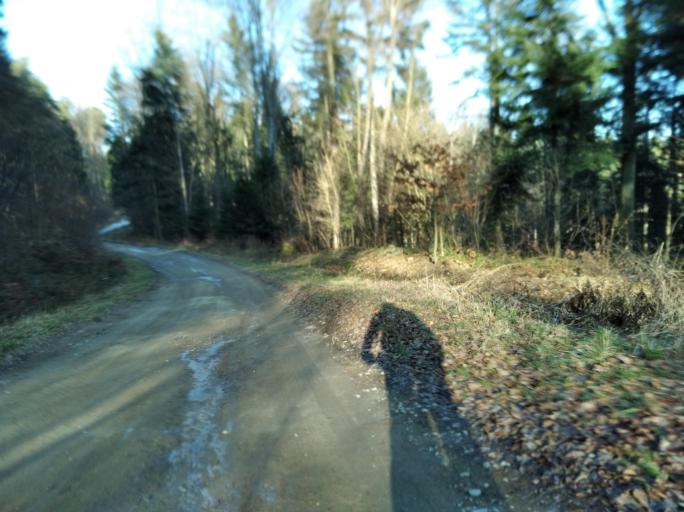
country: PL
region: Subcarpathian Voivodeship
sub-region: Powiat strzyzowski
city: Jawornik
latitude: 49.8322
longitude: 21.8585
